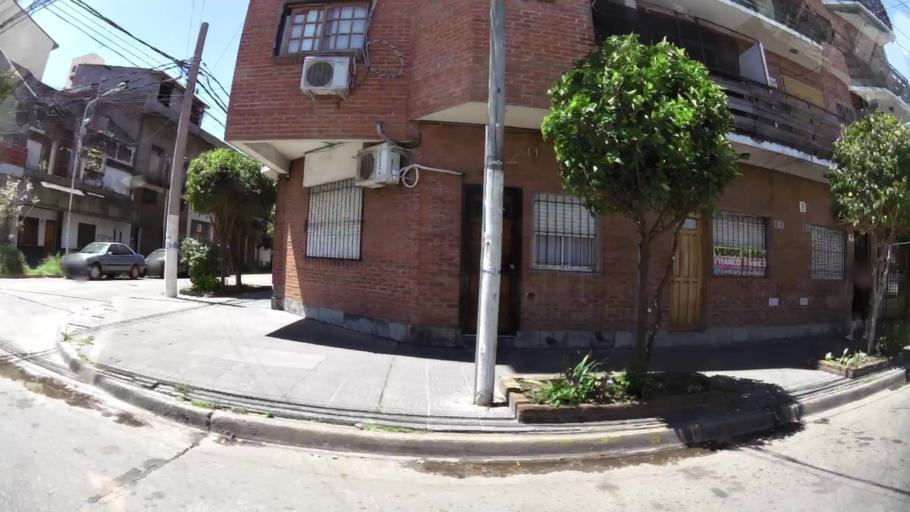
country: AR
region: Buenos Aires
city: Caseros
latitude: -34.5953
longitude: -58.5494
